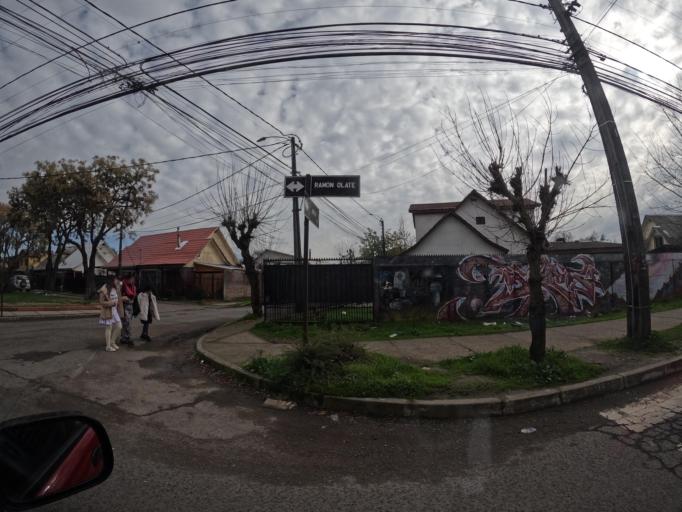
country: CL
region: Maule
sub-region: Provincia de Linares
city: Linares
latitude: -35.8353
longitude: -71.6018
